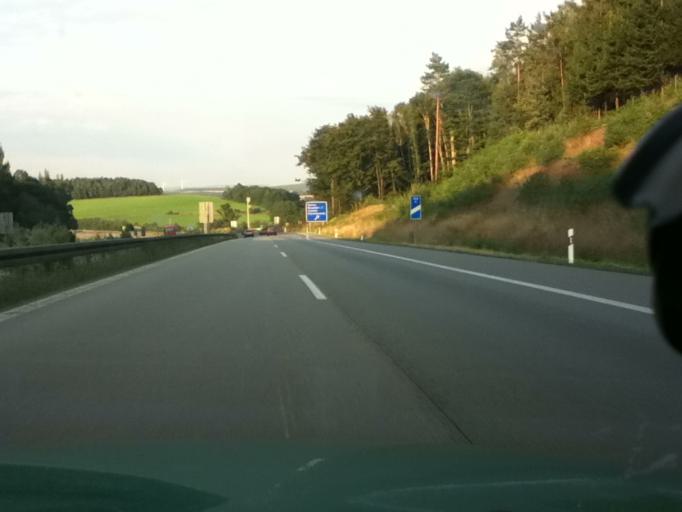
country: DE
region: Saxony
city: Rammenau
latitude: 51.1744
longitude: 14.1332
